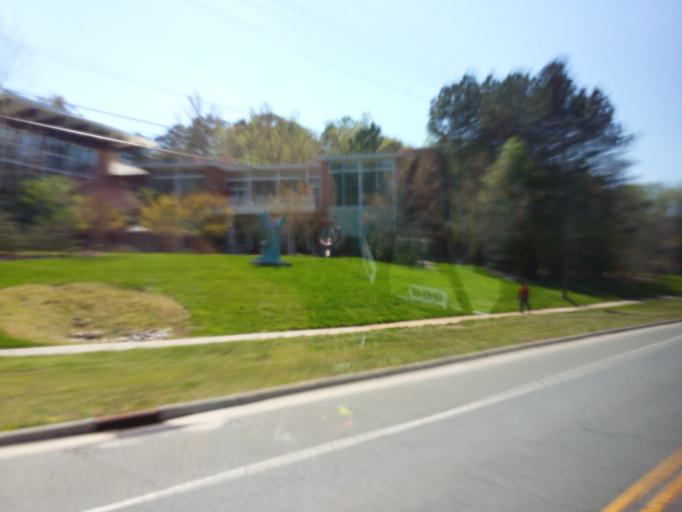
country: US
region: North Carolina
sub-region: Orange County
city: Chapel Hill
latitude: 35.9512
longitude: -79.0631
